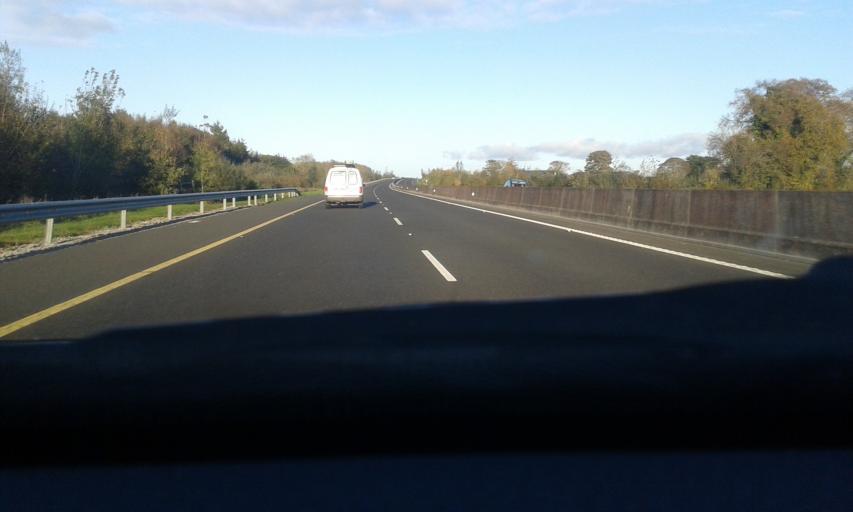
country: IE
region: Munster
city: Thurles
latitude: 52.6859
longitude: -7.6735
